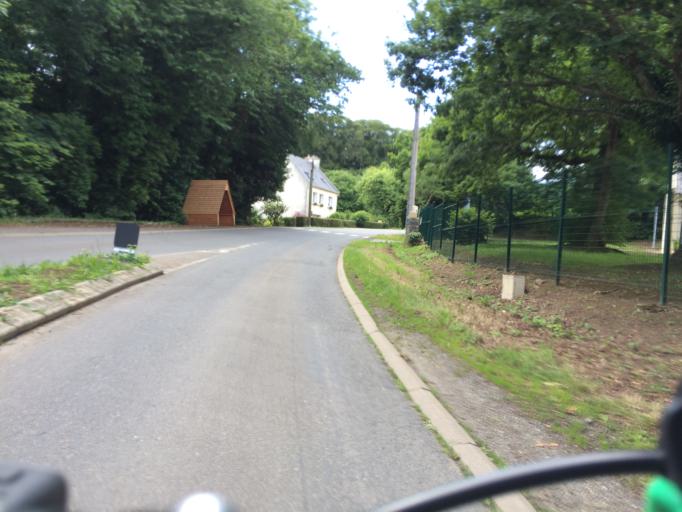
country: FR
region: Brittany
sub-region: Departement du Finistere
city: Logonna-Daoulas
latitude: 48.3217
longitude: -4.2868
